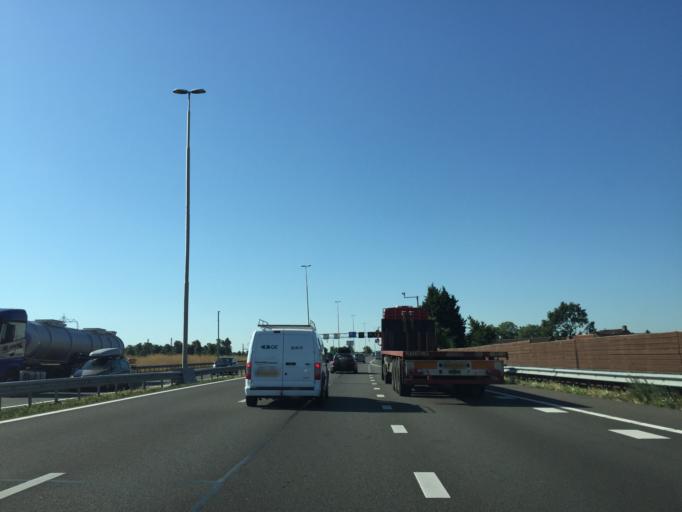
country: NL
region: Limburg
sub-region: Gemeente Sittard-Geleen
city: Born
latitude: 51.0524
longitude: 5.8270
